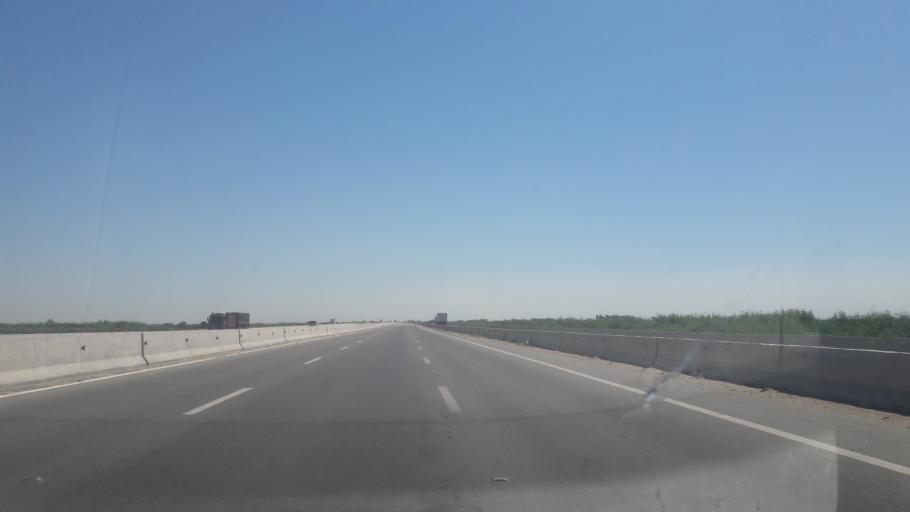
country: EG
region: Muhafazat ad Daqahliyah
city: Al Matariyah
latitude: 30.9152
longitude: 32.1909
